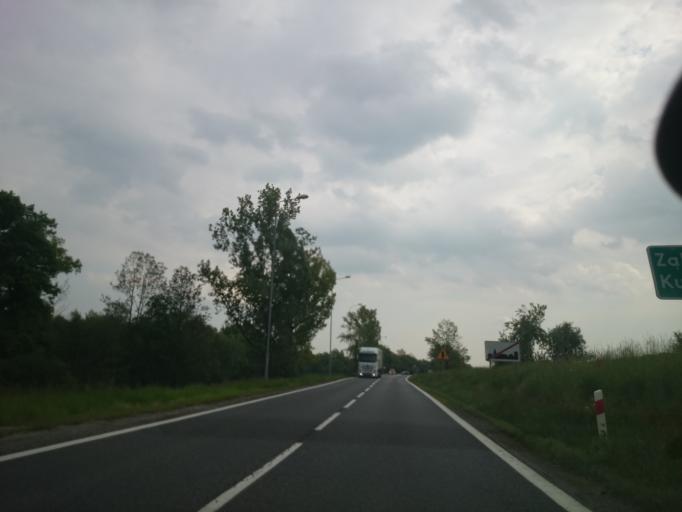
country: PL
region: Lower Silesian Voivodeship
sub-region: Powiat dzierzoniowski
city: Niemcza
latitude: 50.7420
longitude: 16.8399
